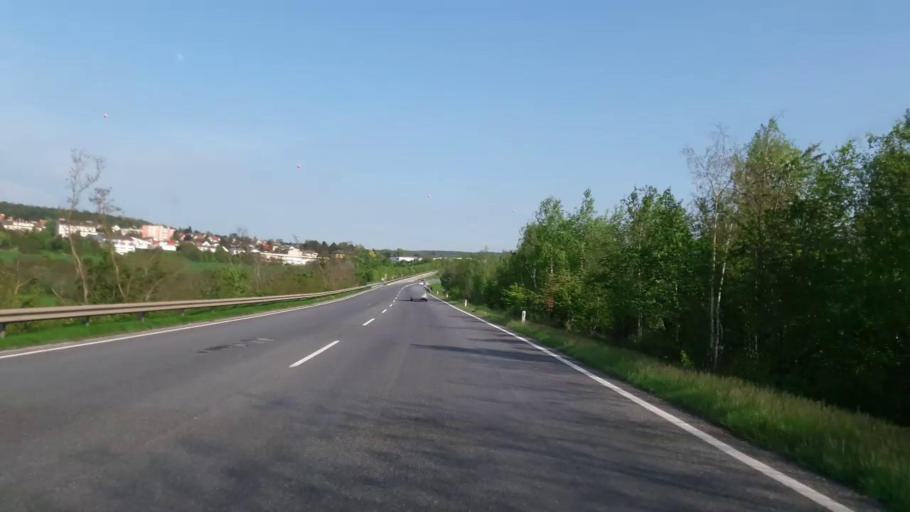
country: AT
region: Lower Austria
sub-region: Politischer Bezirk Hollabrunn
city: Hollabrunn
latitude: 48.5508
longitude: 16.0703
